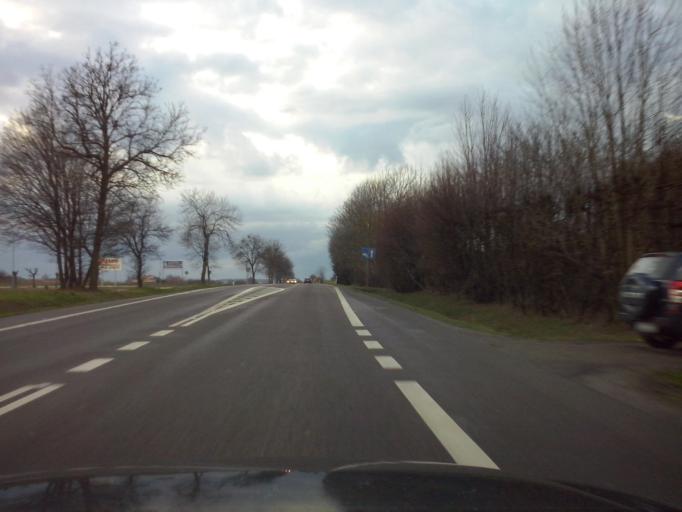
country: PL
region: Lublin Voivodeship
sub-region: Chelm
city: Chelm
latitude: 51.1582
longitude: 23.4013
